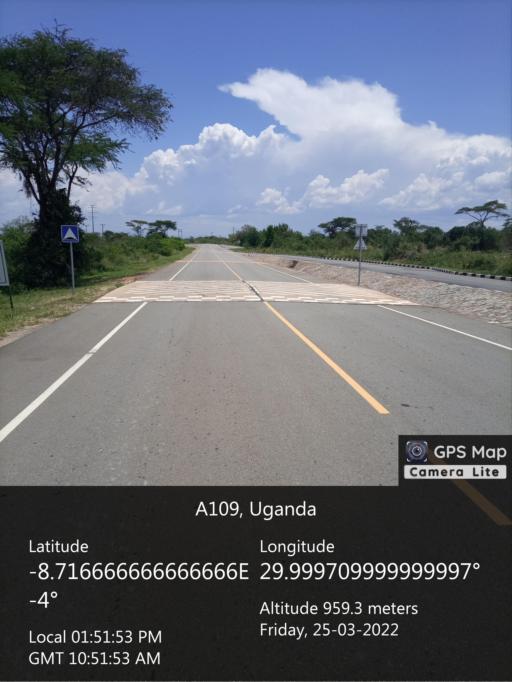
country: UG
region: Western Region
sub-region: Kasese District
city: Kilembe
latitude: -0.0009
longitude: 29.9997
